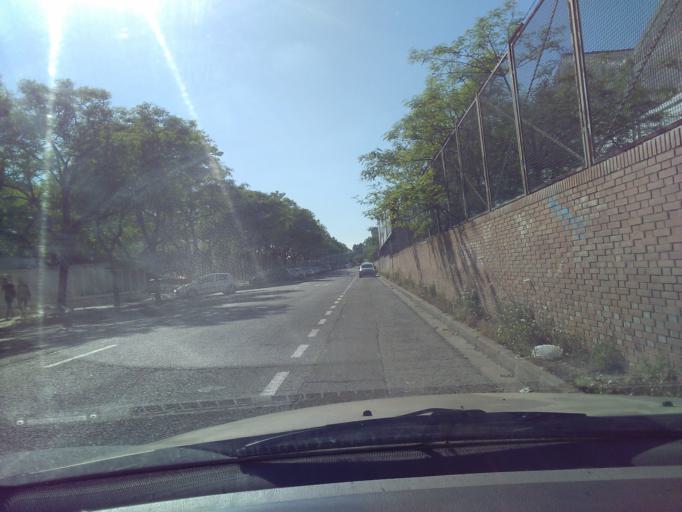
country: ES
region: Andalusia
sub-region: Provincia de Sevilla
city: Sevilla
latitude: 37.4076
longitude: -5.9308
